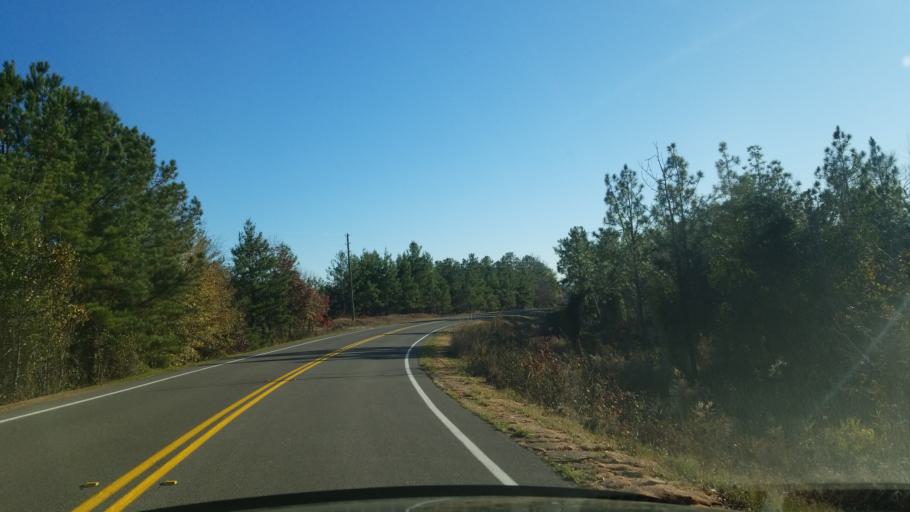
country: US
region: Georgia
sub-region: Talbot County
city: Talbotton
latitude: 32.5744
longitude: -84.5413
